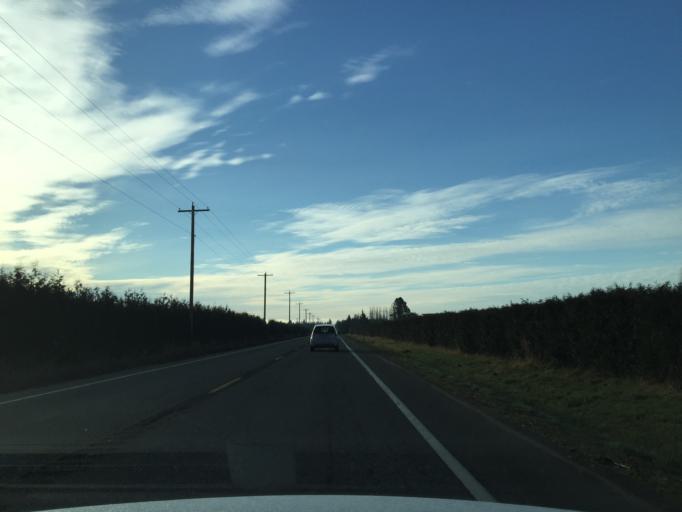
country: US
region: Washington
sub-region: Whatcom County
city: Lynden
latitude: 48.9581
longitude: -122.4853
